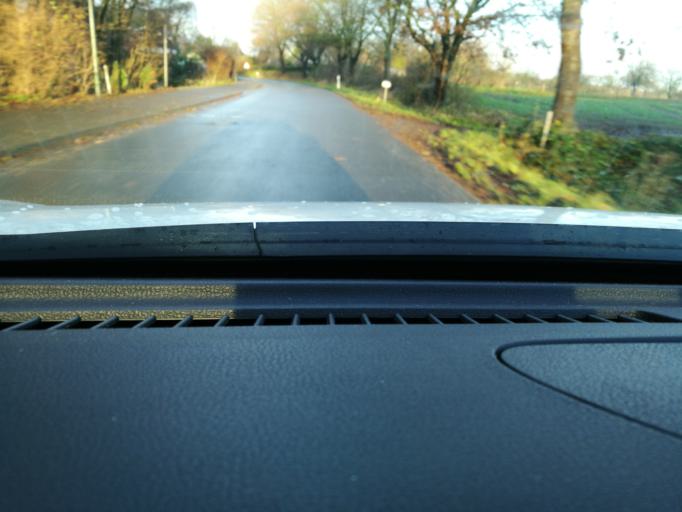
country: DE
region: Schleswig-Holstein
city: Holzbunge
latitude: 54.3974
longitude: 9.7040
